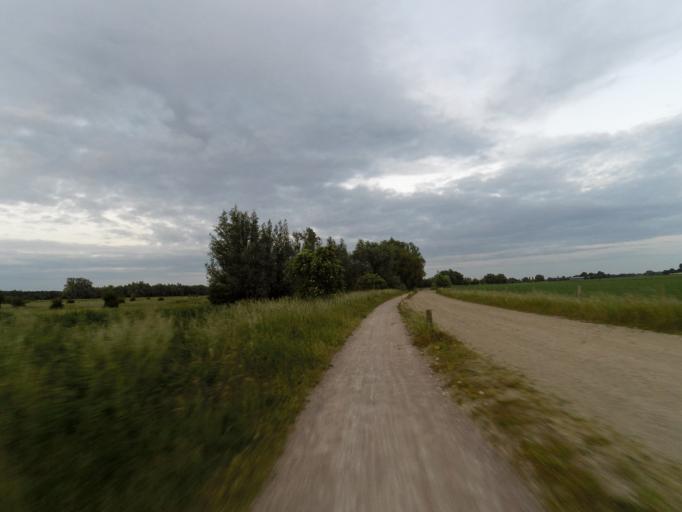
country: NL
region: Gelderland
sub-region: Gemeente Zevenaar
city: Zevenaar
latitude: 51.8852
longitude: 6.1260
